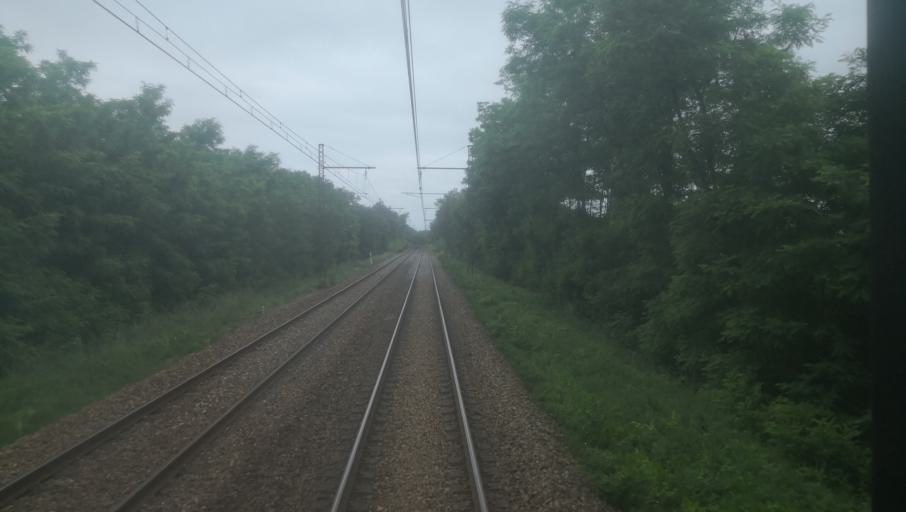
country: FR
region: Centre
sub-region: Departement de l'Indre
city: Le Pechereau
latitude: 46.4981
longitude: 1.5197
